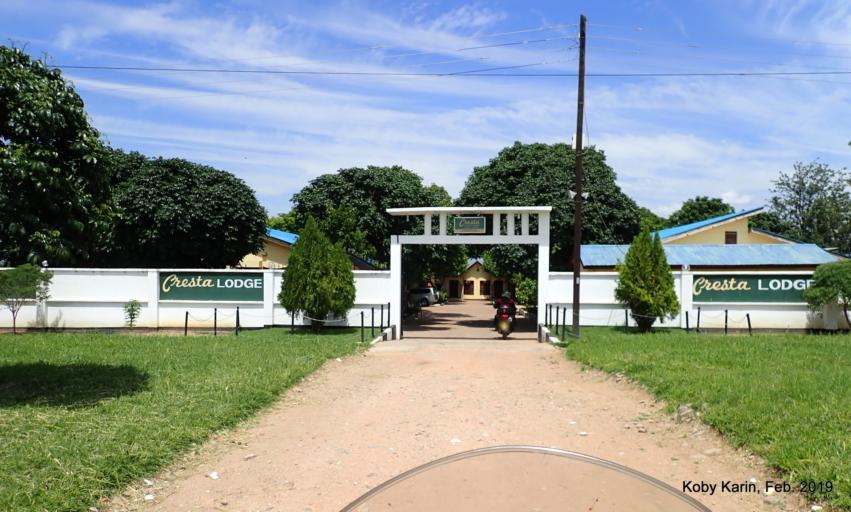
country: TZ
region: Singida
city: Singida
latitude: -4.7973
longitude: 34.7389
